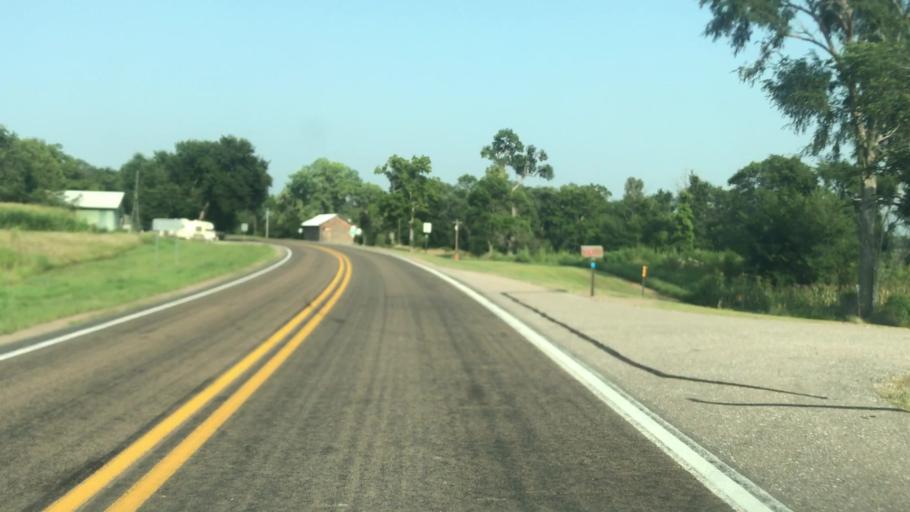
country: US
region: Nebraska
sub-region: Buffalo County
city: Ravenna
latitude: 41.0742
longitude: -98.7246
